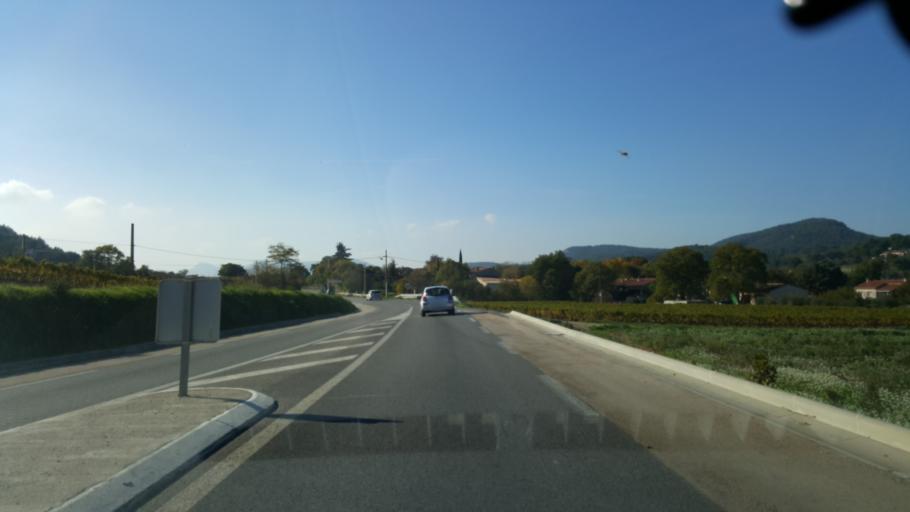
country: FR
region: Provence-Alpes-Cote d'Azur
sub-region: Departement du Var
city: Saint-Zacharie
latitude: 43.3773
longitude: 5.6806
